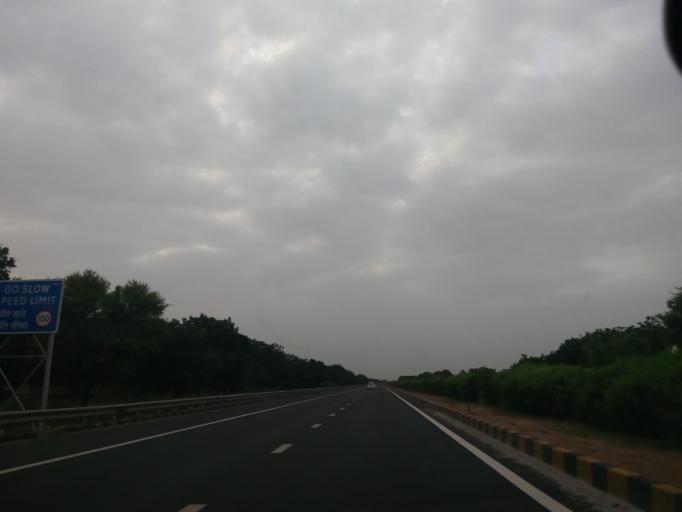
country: IN
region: Gujarat
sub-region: Kheda
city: Mahemdavad
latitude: 22.9237
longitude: 72.7467
